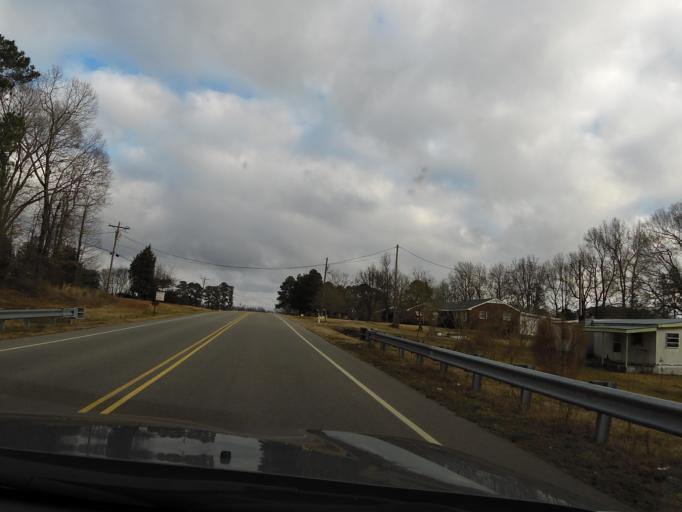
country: US
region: North Carolina
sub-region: Edgecombe County
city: Pinetops
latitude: 35.8119
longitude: -77.6550
